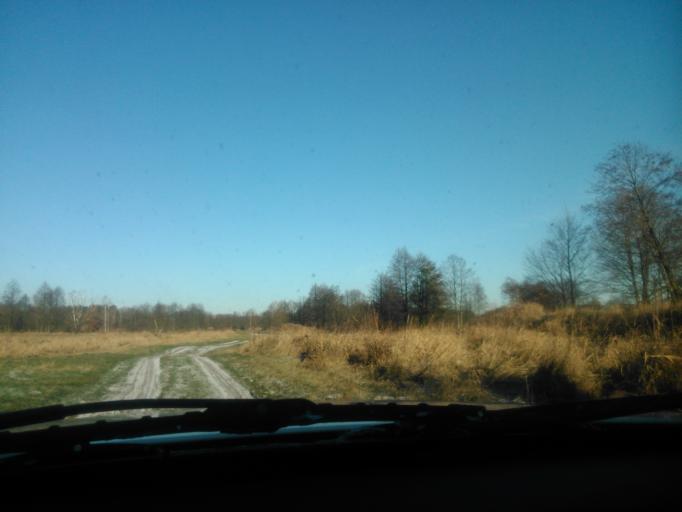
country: PL
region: Warmian-Masurian Voivodeship
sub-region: Powiat nowomiejski
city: Kurzetnik
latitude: 53.3654
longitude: 19.5246
